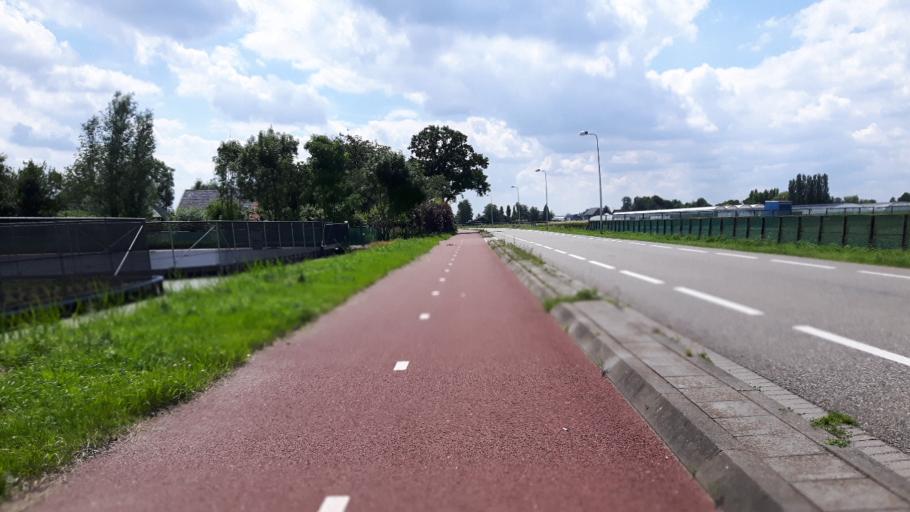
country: NL
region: South Holland
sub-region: Bodegraven-Reeuwijk
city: Reeuwijk
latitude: 52.0866
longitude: 4.7014
